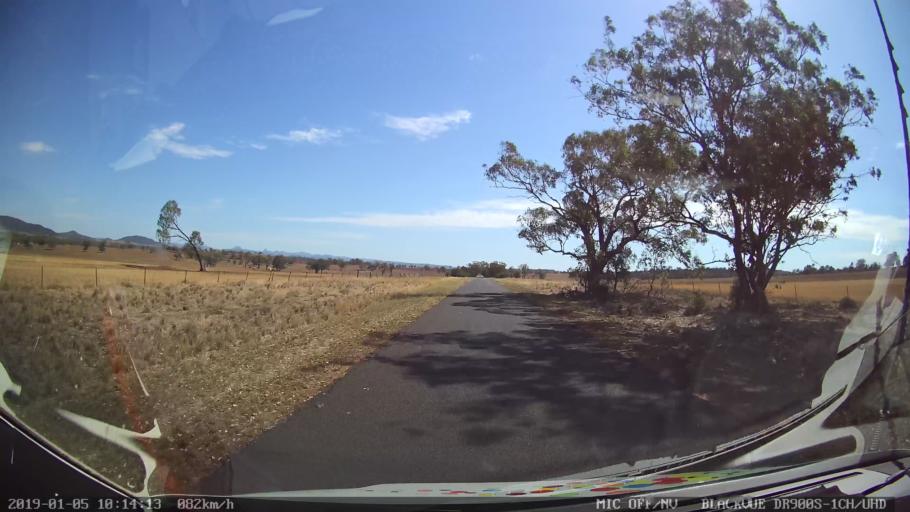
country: AU
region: New South Wales
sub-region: Gilgandra
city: Gilgandra
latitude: -31.5949
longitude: 148.9323
